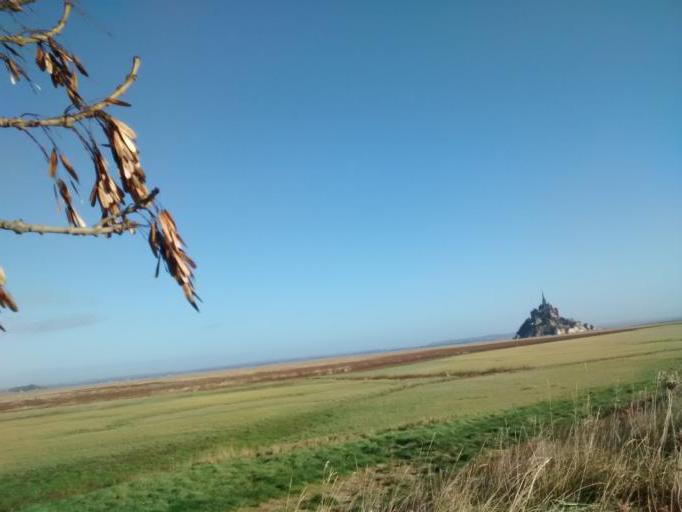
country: FR
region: Brittany
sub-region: Departement d'Ille-et-Vilaine
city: Roz-sur-Couesnon
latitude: 48.6307
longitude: -1.5380
